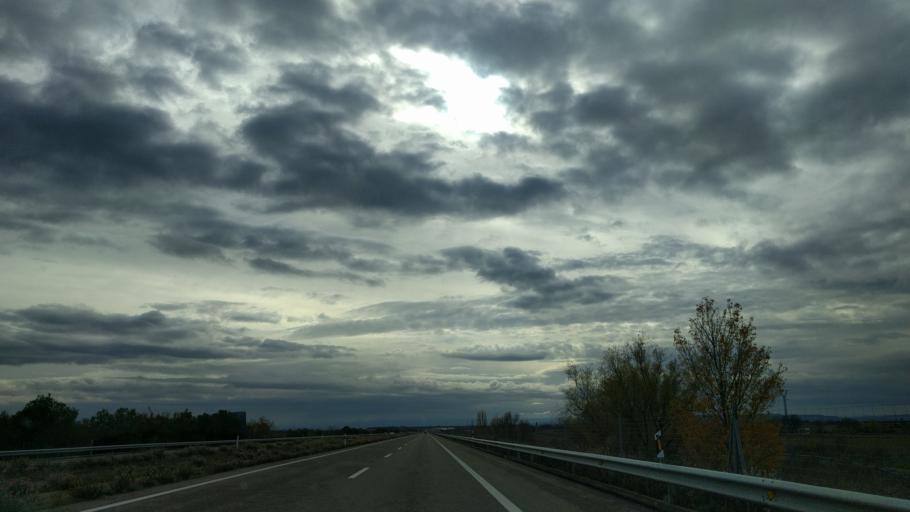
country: ES
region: Aragon
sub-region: Provincia de Huesca
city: Igries
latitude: 42.2051
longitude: -0.4358
